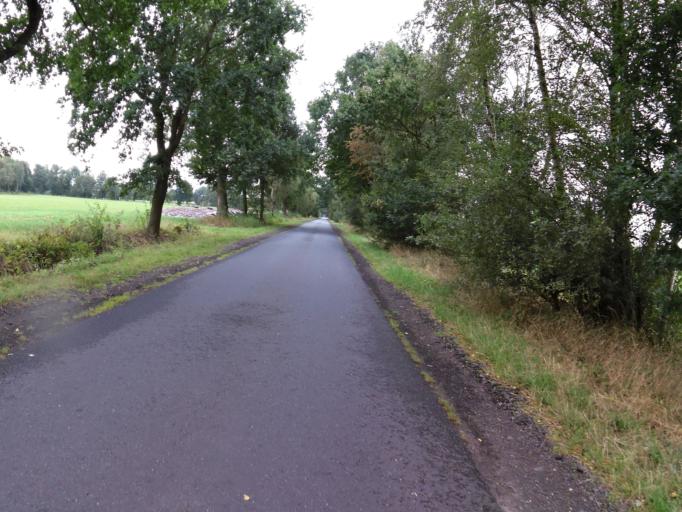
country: DE
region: Lower Saxony
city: Helvesiek
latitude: 53.2055
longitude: 9.4608
